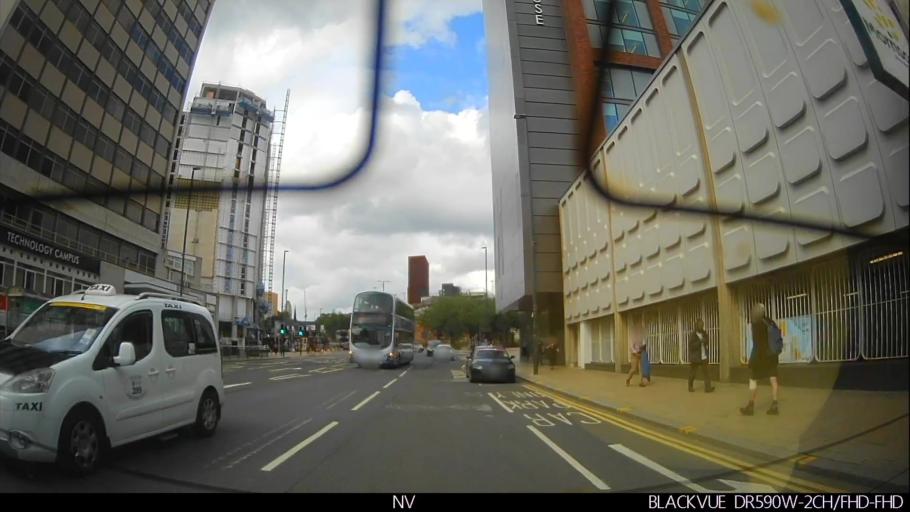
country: GB
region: England
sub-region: City and Borough of Leeds
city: Leeds
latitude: 53.8022
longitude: -1.5455
